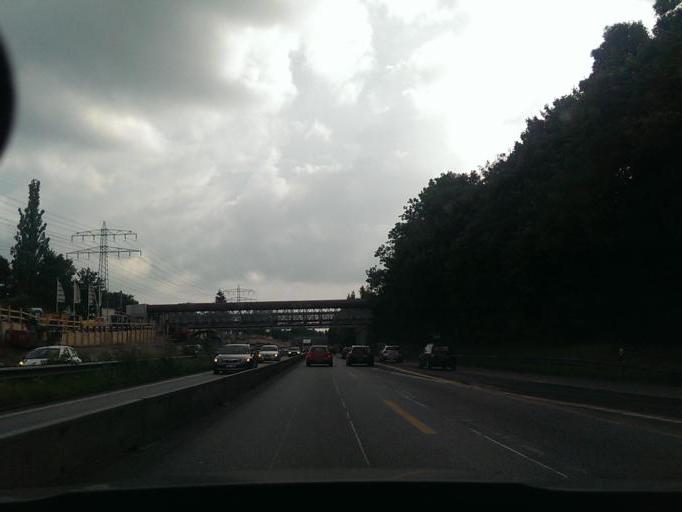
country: DE
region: Hamburg
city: Eidelstedt
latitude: 53.6330
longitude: 9.9231
